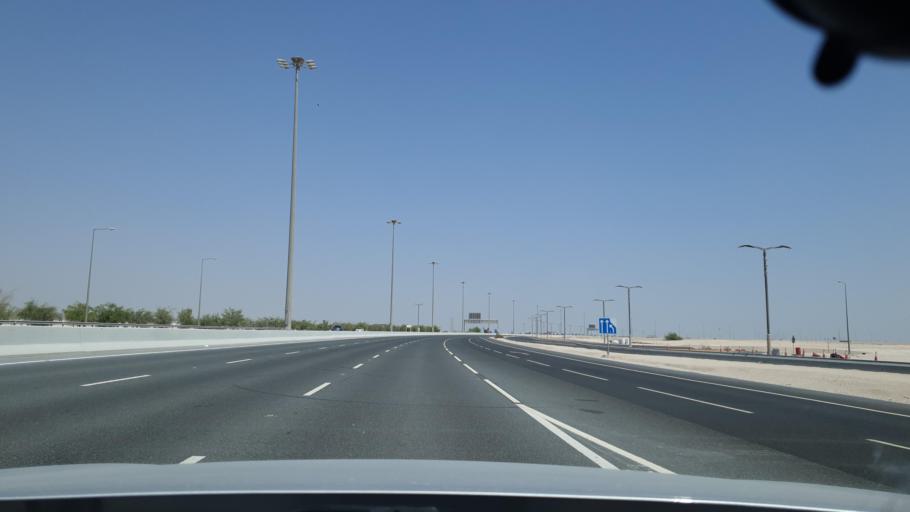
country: QA
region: Baladiyat Umm Salal
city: Umm Salal Muhammad
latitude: 25.3621
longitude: 51.3669
